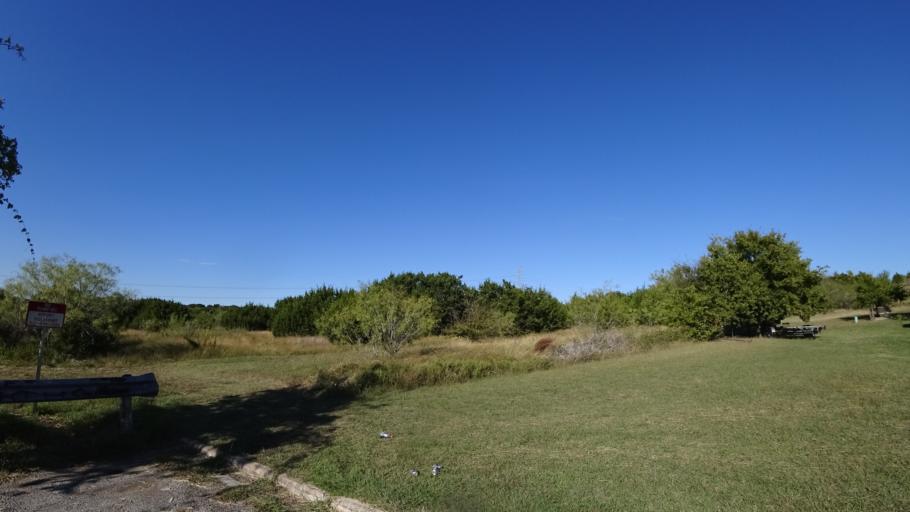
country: US
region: Texas
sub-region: Travis County
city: Hornsby Bend
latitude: 30.2997
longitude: -97.6284
